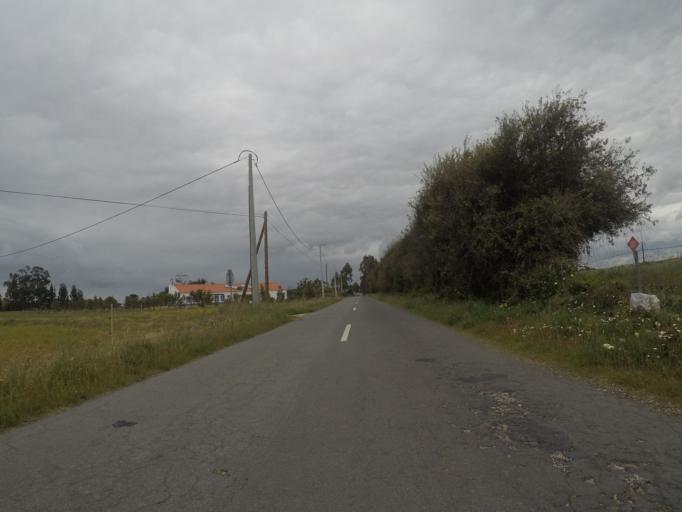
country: PT
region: Beja
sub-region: Odemira
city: Sao Teotonio
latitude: 37.5867
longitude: -8.7780
